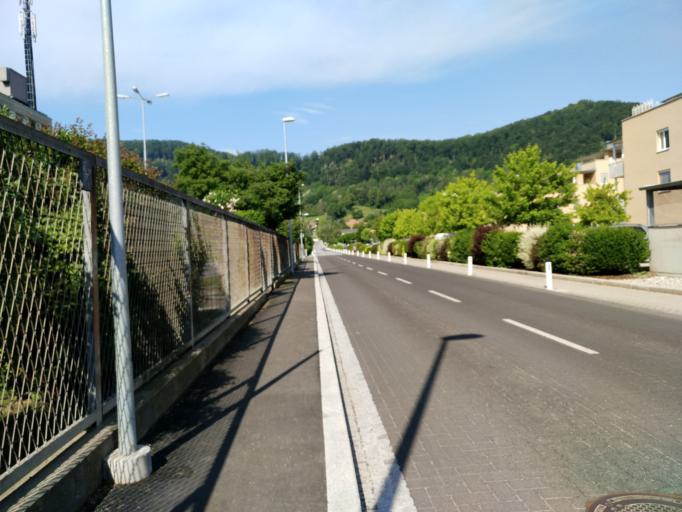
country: AT
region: Styria
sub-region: Graz Stadt
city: Wetzelsdorf
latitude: 47.0466
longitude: 15.3938
